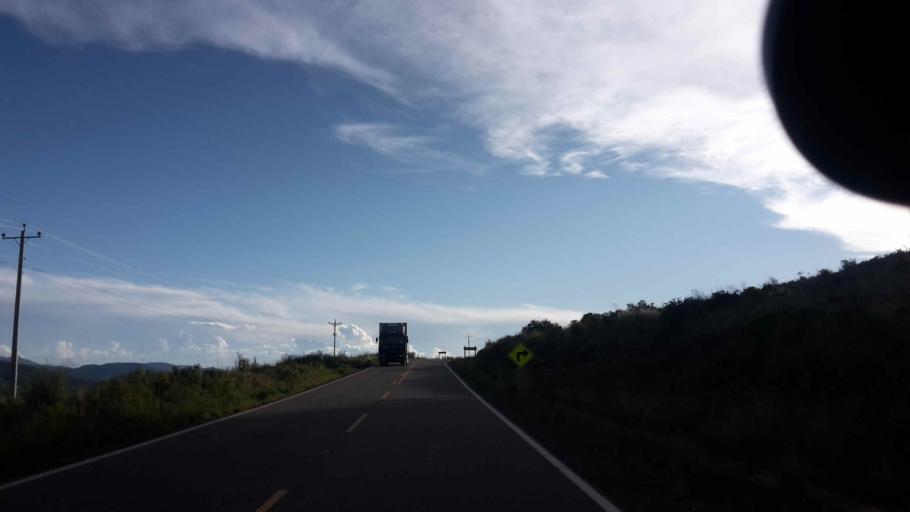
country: BO
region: Cochabamba
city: Arani
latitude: -17.5570
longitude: -65.6990
